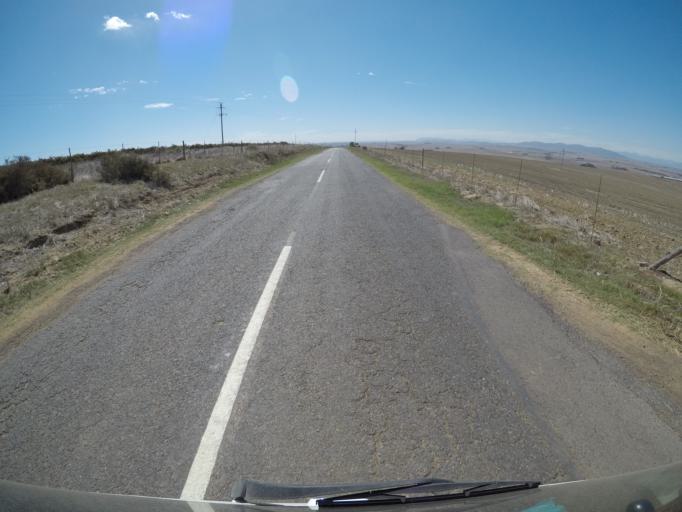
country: ZA
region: Western Cape
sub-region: City of Cape Town
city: Sunset Beach
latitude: -33.7118
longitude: 18.5823
